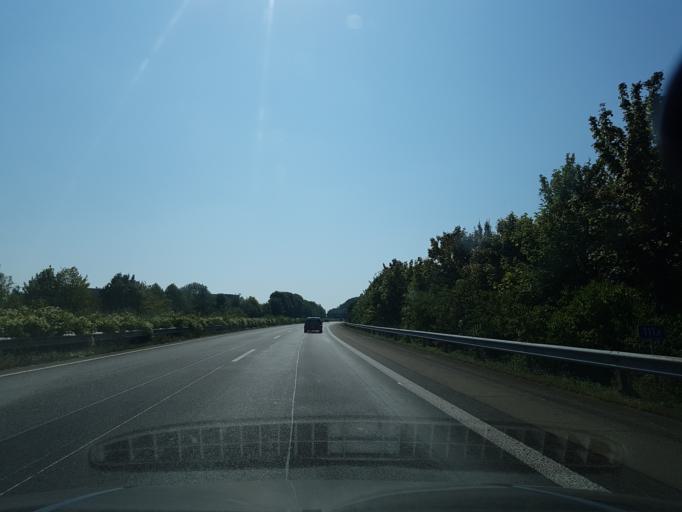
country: DE
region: Rheinland-Pfalz
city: Contwig
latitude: 49.2264
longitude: 7.4349
